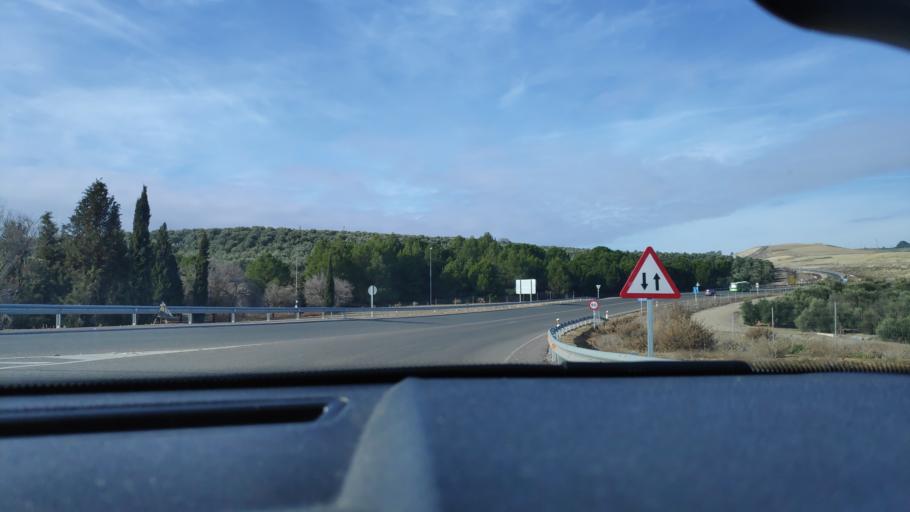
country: ES
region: Andalusia
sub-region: Provincia de Jaen
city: Linares
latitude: 38.0744
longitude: -3.5915
